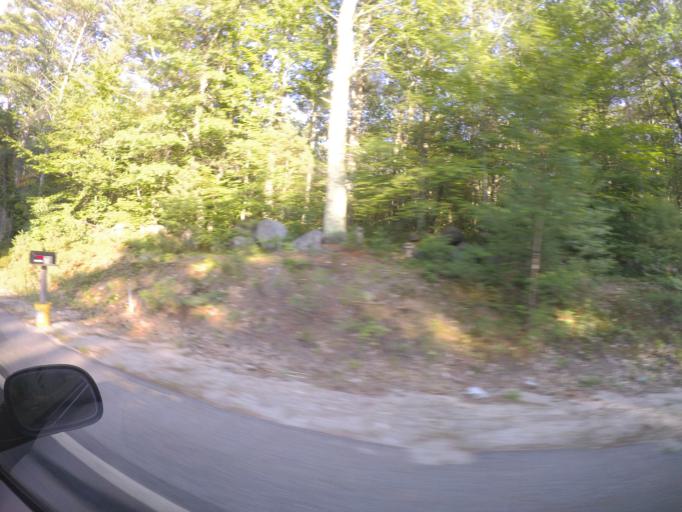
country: US
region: Maine
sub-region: Cumberland County
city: Raymond
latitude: 43.8961
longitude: -70.4557
